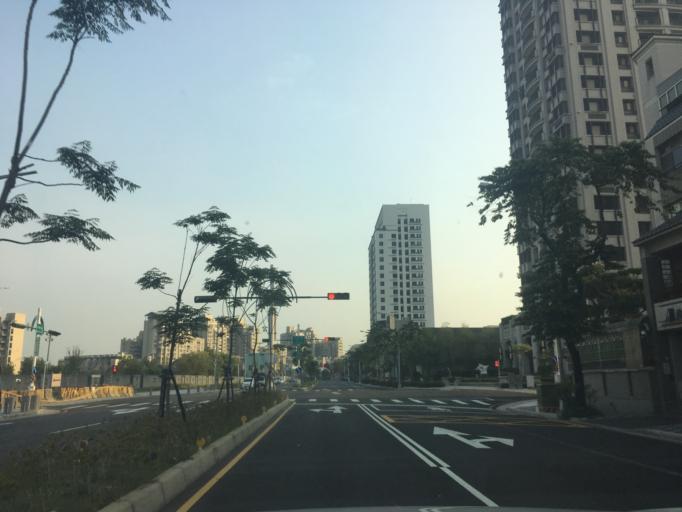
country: TW
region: Taiwan
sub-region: Taichung City
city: Taichung
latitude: 24.1850
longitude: 120.6823
